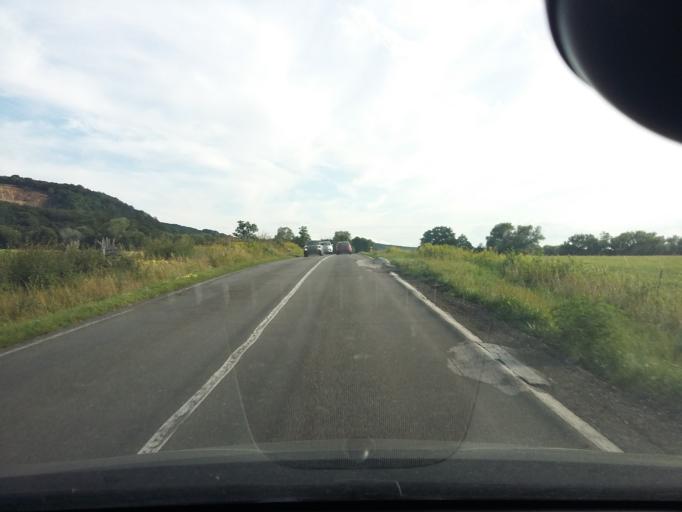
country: SK
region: Bratislavsky
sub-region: Okres Malacky
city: Malacky
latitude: 48.3824
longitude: 17.1527
